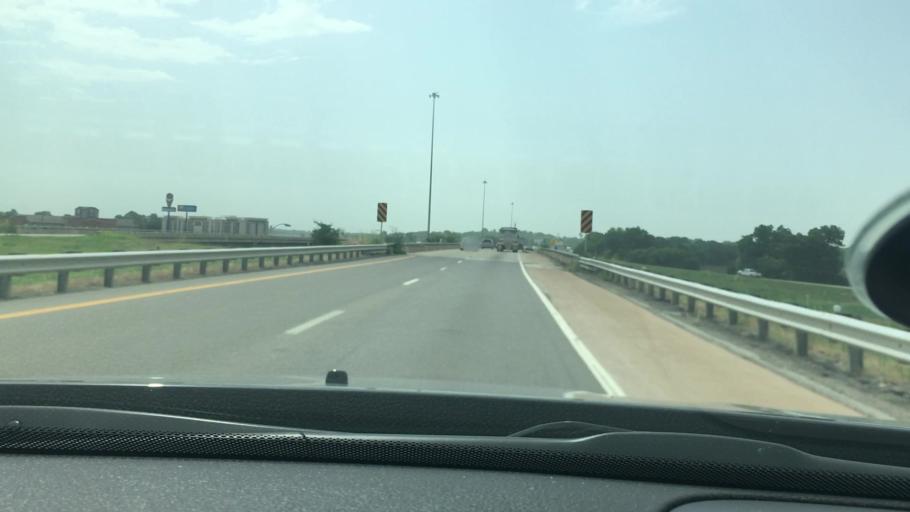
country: US
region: Oklahoma
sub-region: Garvin County
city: Pauls Valley
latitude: 34.7400
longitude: -97.2638
